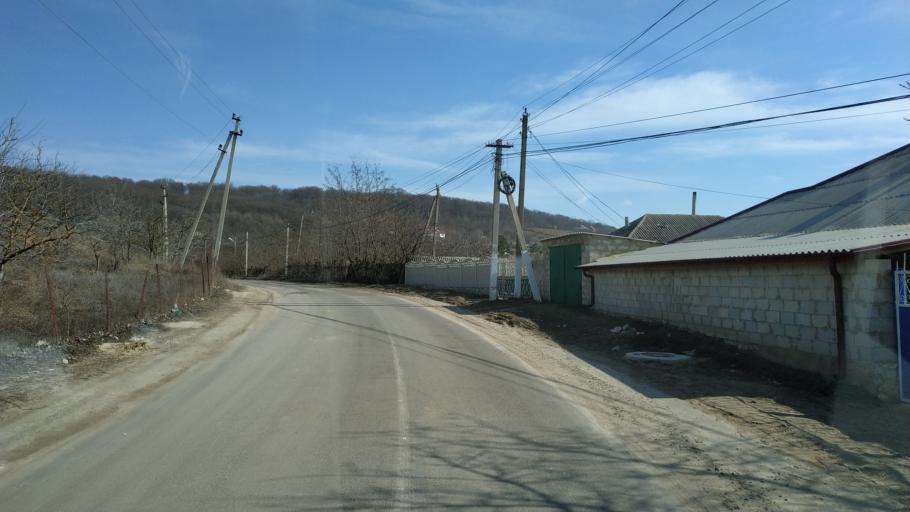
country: MD
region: Nisporeni
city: Nisporeni
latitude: 47.2210
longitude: 28.0496
